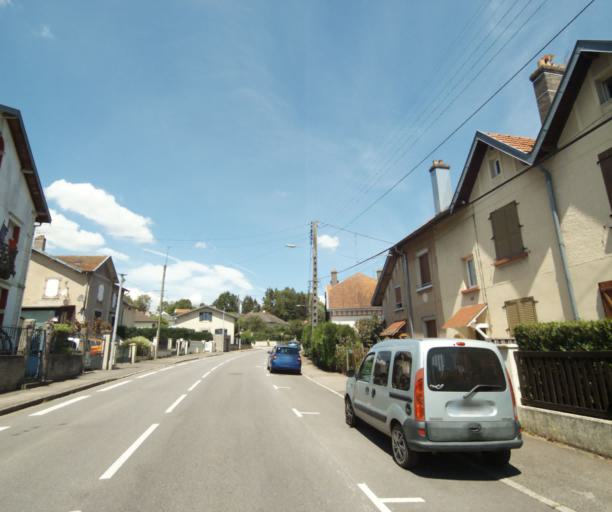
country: FR
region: Lorraine
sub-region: Departement de Meurthe-et-Moselle
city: Luneville
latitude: 48.6035
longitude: 6.4881
